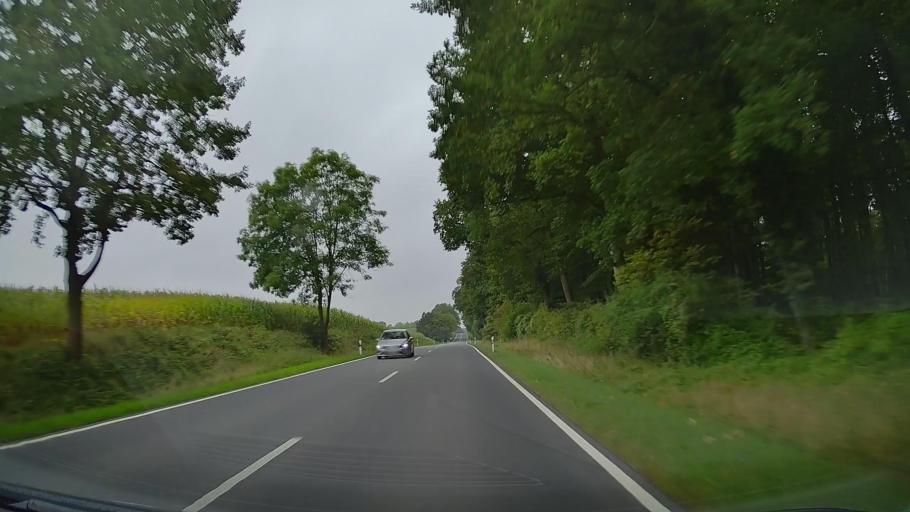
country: DE
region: Mecklenburg-Vorpommern
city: Tarnow
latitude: 53.7442
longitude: 12.0140
